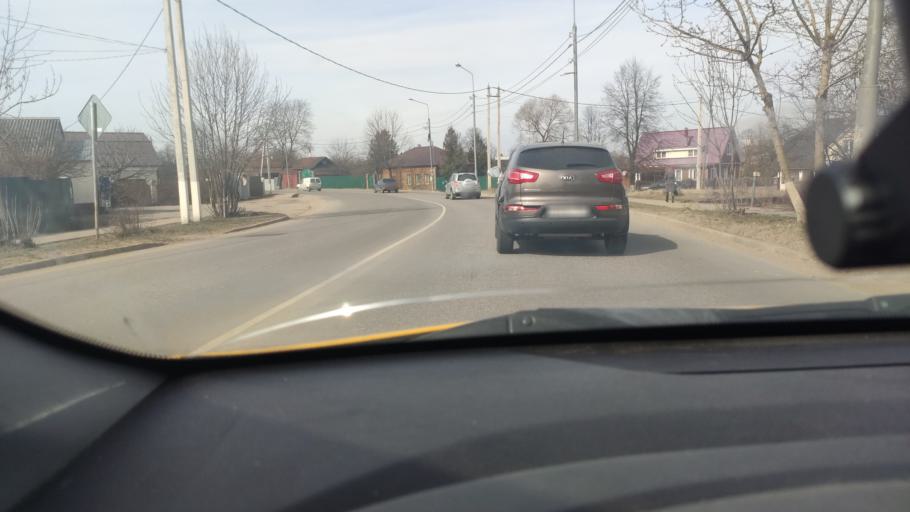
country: RU
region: Moskovskaya
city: Ruza
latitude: 55.6955
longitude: 36.2051
